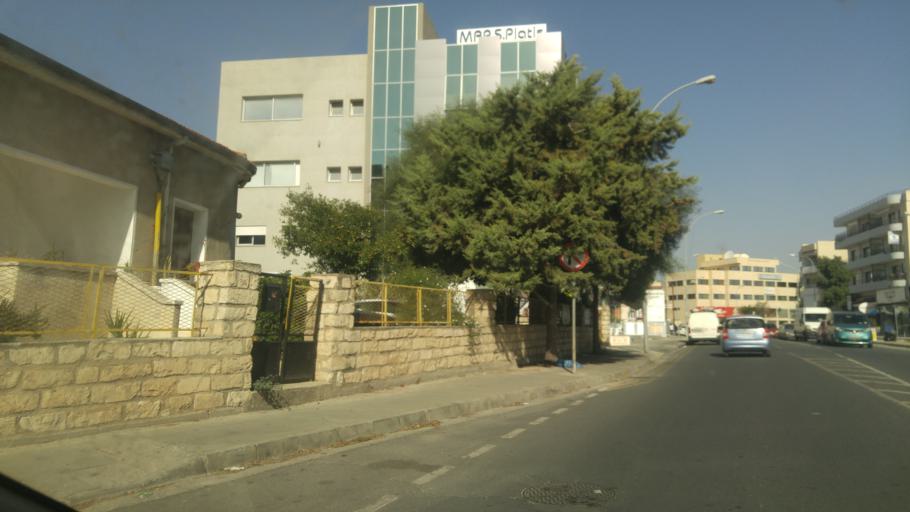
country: CY
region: Limassol
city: Limassol
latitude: 34.6999
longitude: 33.0457
